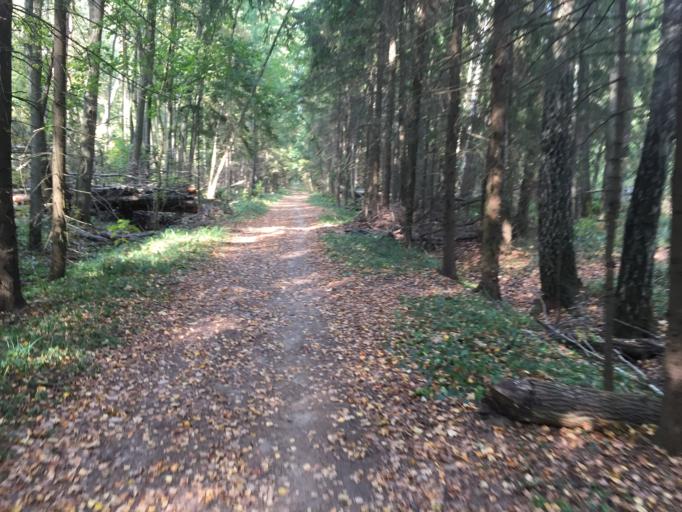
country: RU
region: Moscow
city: Babushkin
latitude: 55.8538
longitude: 37.7438
